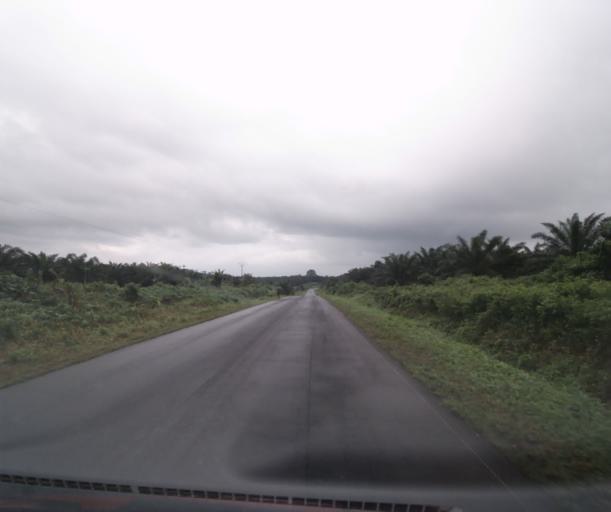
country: CM
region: South-West Province
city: Idenao
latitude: 4.1444
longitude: 8.9902
